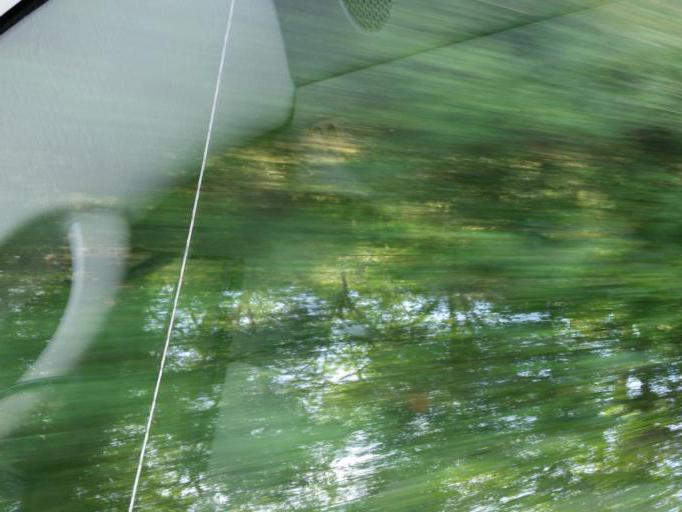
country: US
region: Georgia
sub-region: Turner County
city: Ashburn
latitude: 31.6932
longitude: -83.6420
